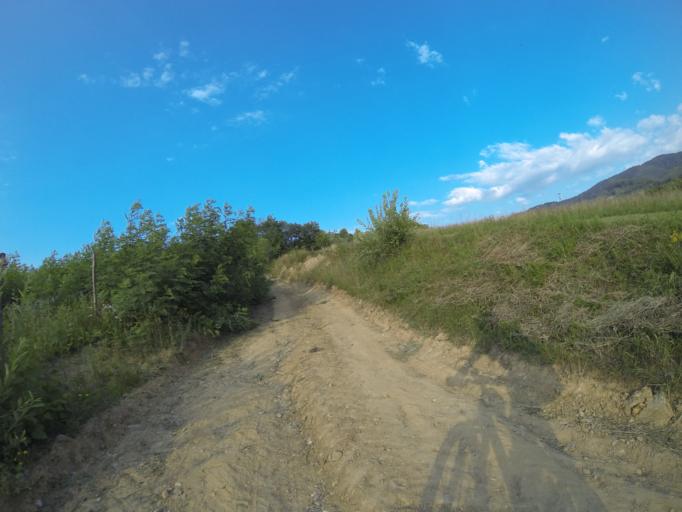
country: RO
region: Brasov
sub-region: Comuna Sinca Noua
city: Sinca Noua
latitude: 45.7146
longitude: 25.2504
